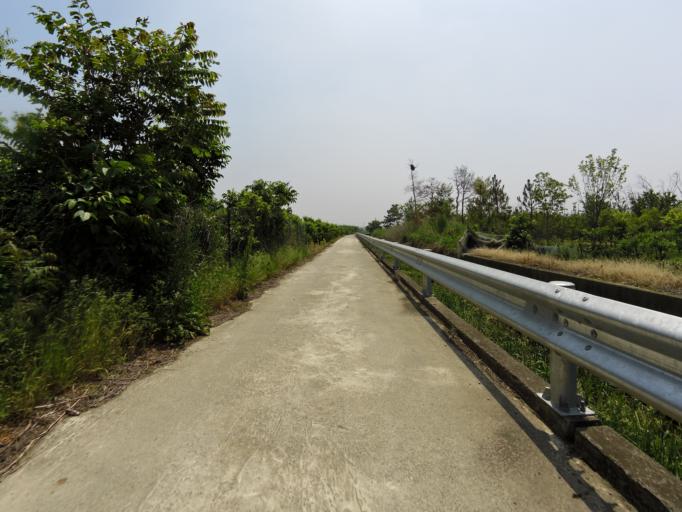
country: KR
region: Gyeongsangbuk-do
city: Gyeongsan-si
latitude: 35.8502
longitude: 128.7291
